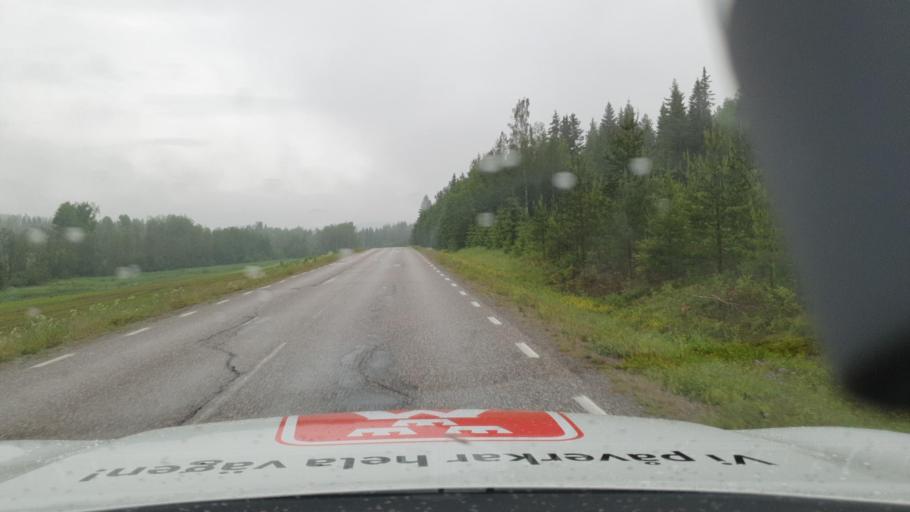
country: SE
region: Vaesterbotten
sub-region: Vannas Kommun
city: Vaennaes
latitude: 63.7766
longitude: 19.6023
